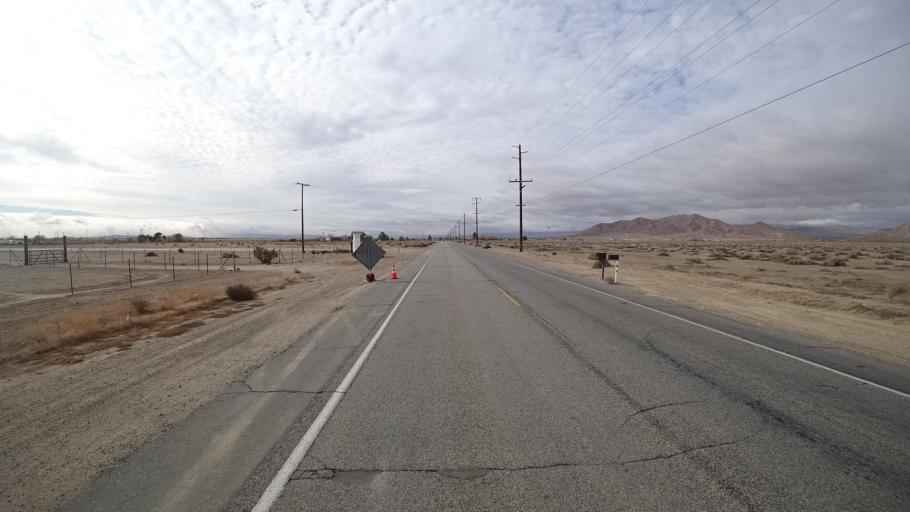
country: US
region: California
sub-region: Kern County
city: Rosamond
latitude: 34.8637
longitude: -118.2418
